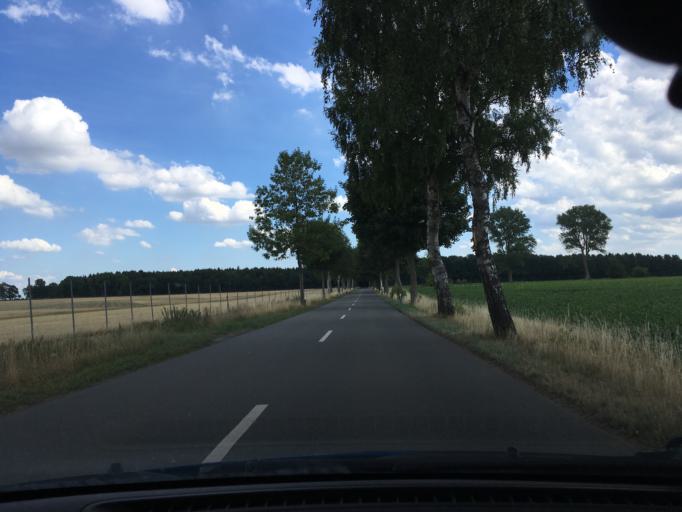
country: DE
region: Lower Saxony
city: Wriedel
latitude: 53.0519
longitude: 10.2504
